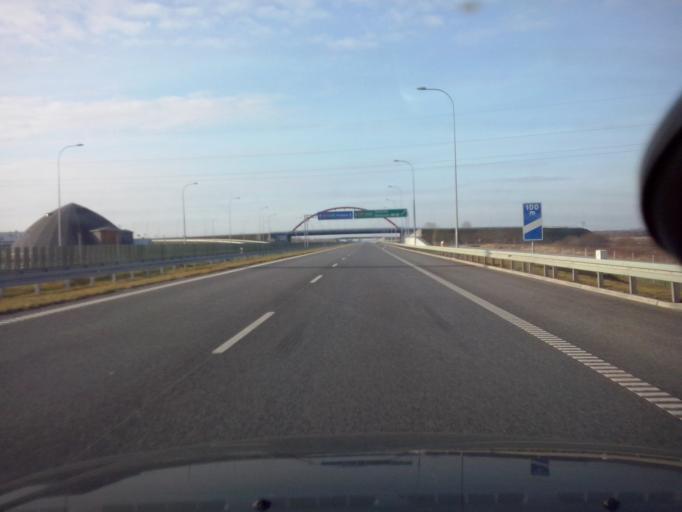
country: PL
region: Subcarpathian Voivodeship
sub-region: Powiat rzeszowski
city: Rudna Wielka
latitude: 50.1054
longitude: 21.9259
